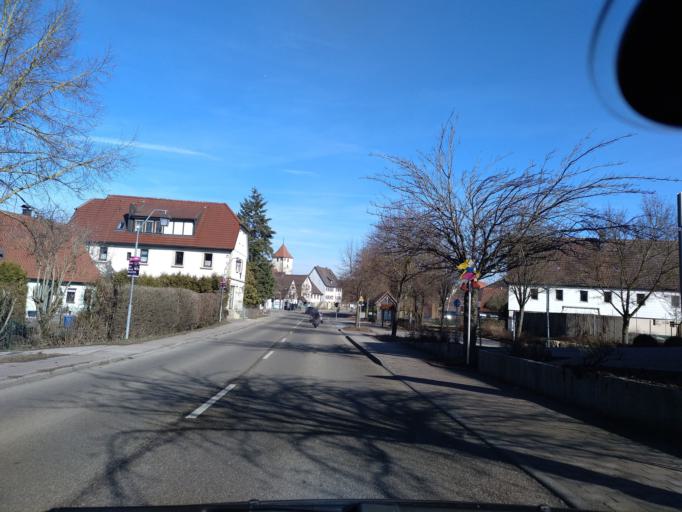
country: DE
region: Baden-Wuerttemberg
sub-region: Regierungsbezirk Stuttgart
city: Michelfeld
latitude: 49.0960
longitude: 9.6758
